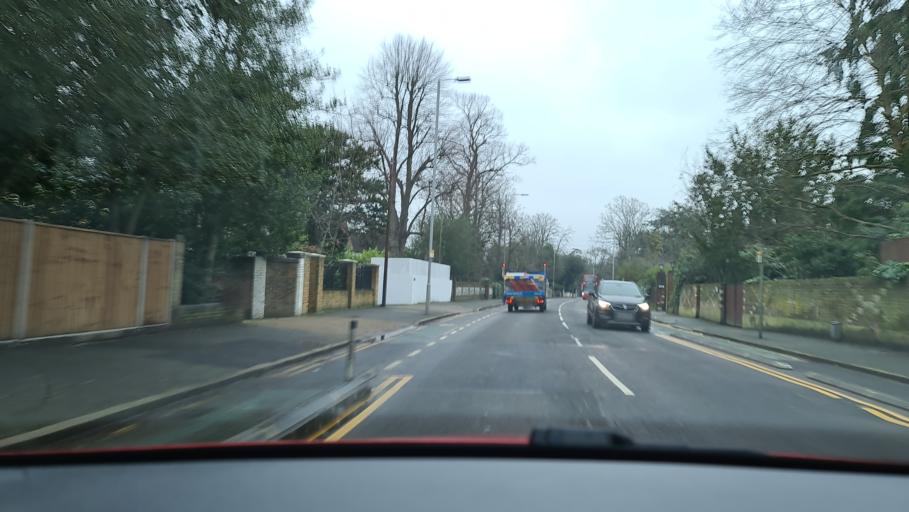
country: GB
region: England
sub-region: Greater London
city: Kingston upon Thames
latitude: 51.4261
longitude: -0.2738
